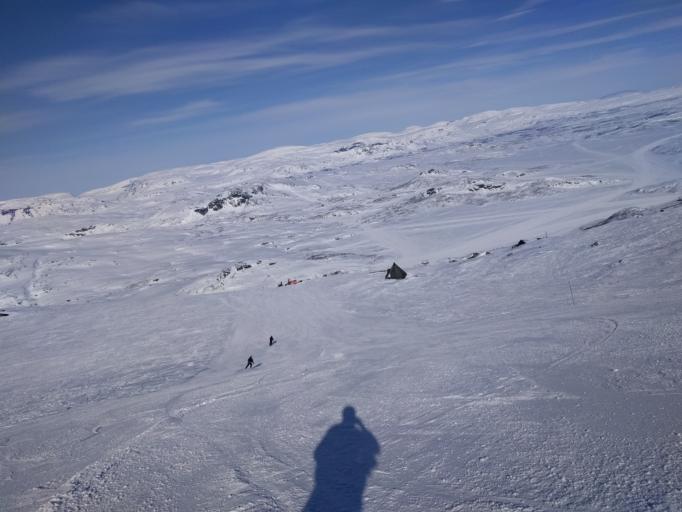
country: NO
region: Troms
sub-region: Lavangen
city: Tennevoll
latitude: 68.4201
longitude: 18.1025
